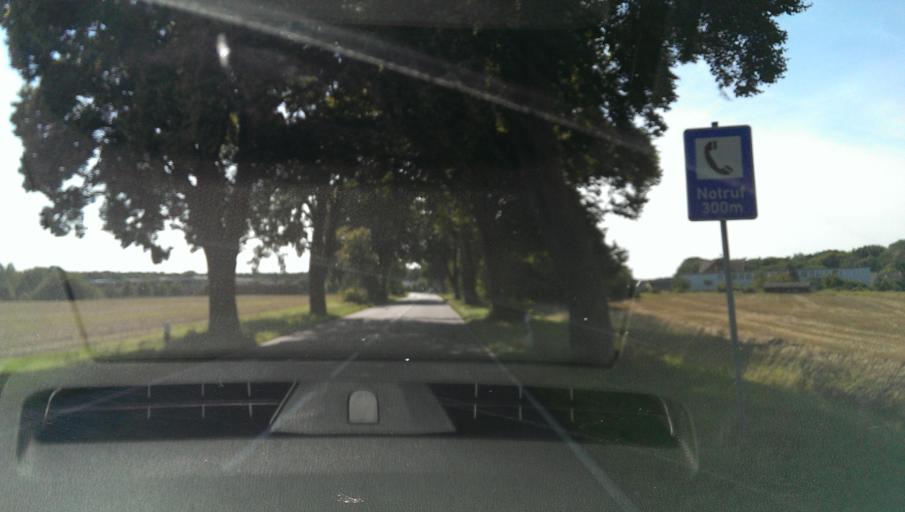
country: DE
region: Saxony-Anhalt
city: Kropstadt
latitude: 51.9612
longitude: 12.7503
